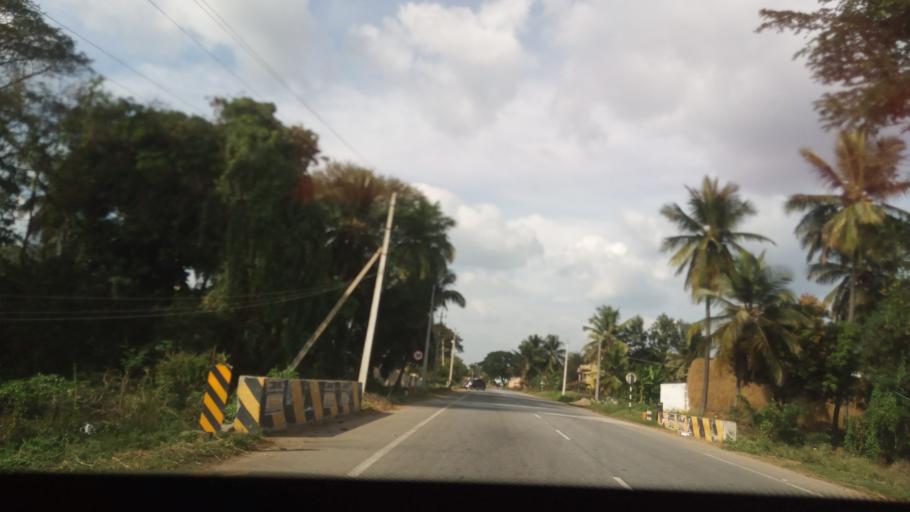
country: IN
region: Karnataka
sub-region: Mandya
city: Maddur
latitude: 12.6245
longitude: 77.0579
